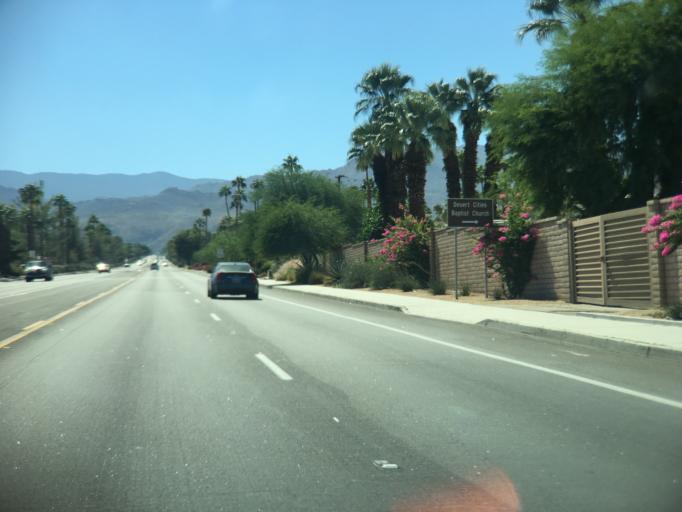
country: US
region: California
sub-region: Riverside County
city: Palm Desert
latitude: 33.7177
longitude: -116.3916
